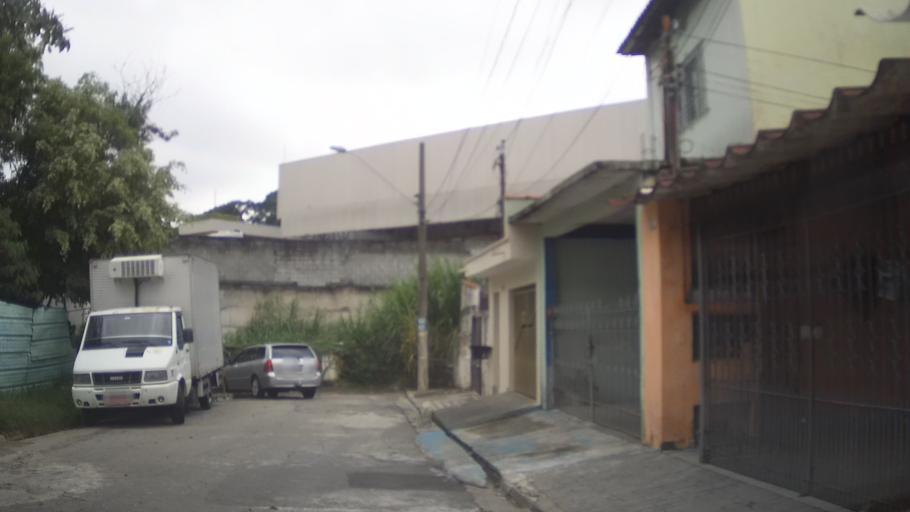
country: BR
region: Sao Paulo
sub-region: Guarulhos
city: Guarulhos
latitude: -23.4838
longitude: -46.5471
